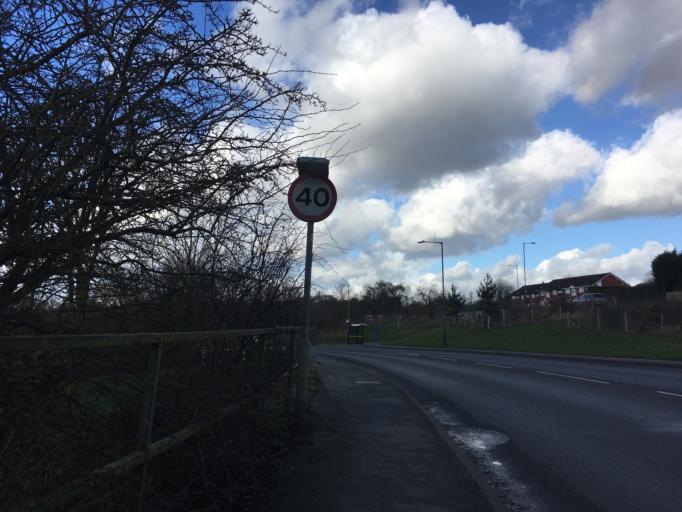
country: GB
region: England
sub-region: Warwickshire
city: Rugby
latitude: 52.3880
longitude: -1.2495
